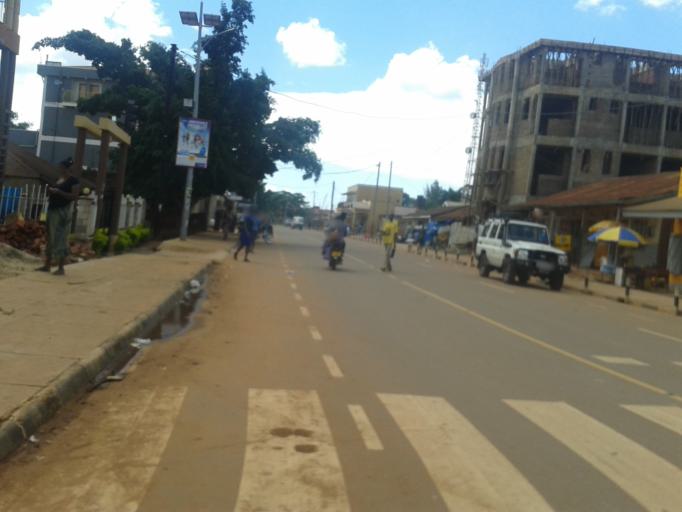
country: UG
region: Northern Region
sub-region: Gulu District
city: Gulu
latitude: 2.7691
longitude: 32.2998
